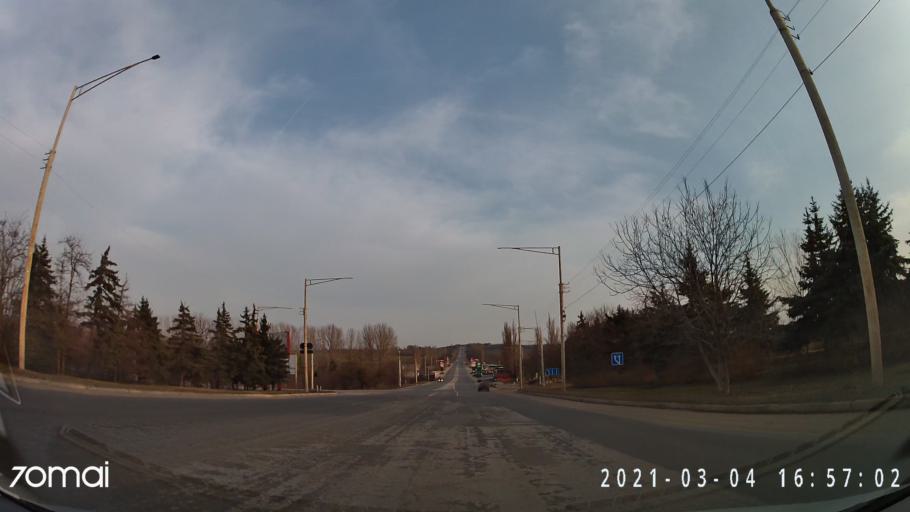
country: MD
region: Balti
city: Balti
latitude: 47.7428
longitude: 27.9551
